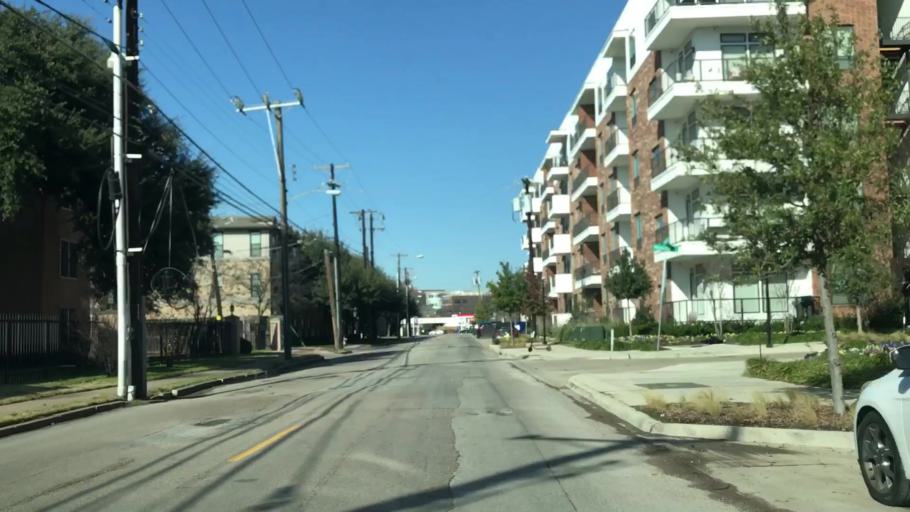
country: US
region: Texas
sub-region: Dallas County
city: Highland Park
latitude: 32.8136
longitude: -96.7848
